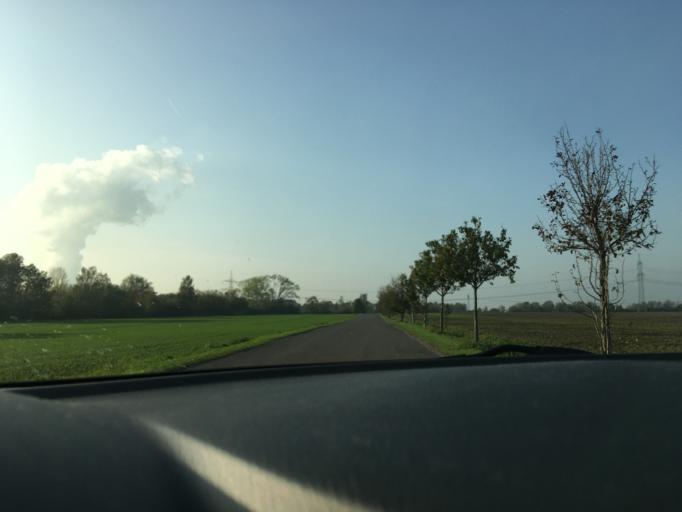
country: DE
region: Saxony
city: Neukieritzsch
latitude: 51.1838
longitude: 12.4351
